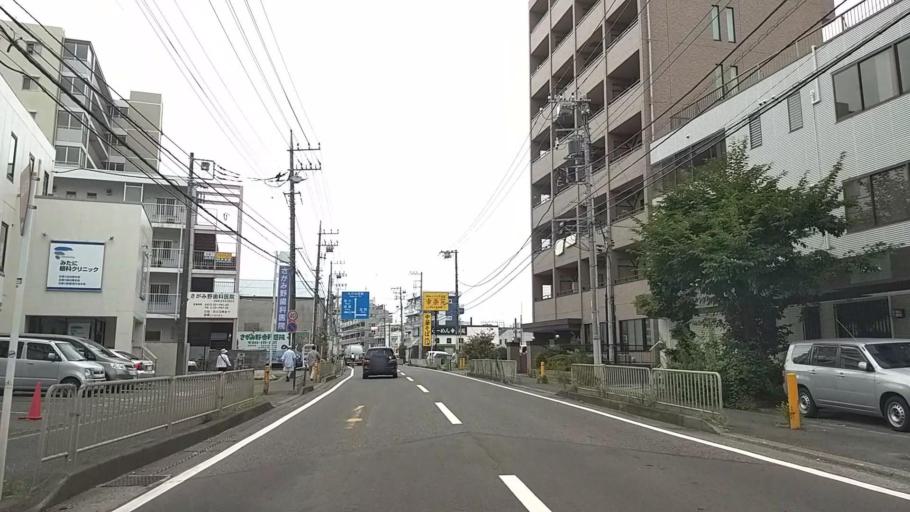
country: JP
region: Kanagawa
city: Minami-rinkan
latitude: 35.4711
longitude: 139.4329
